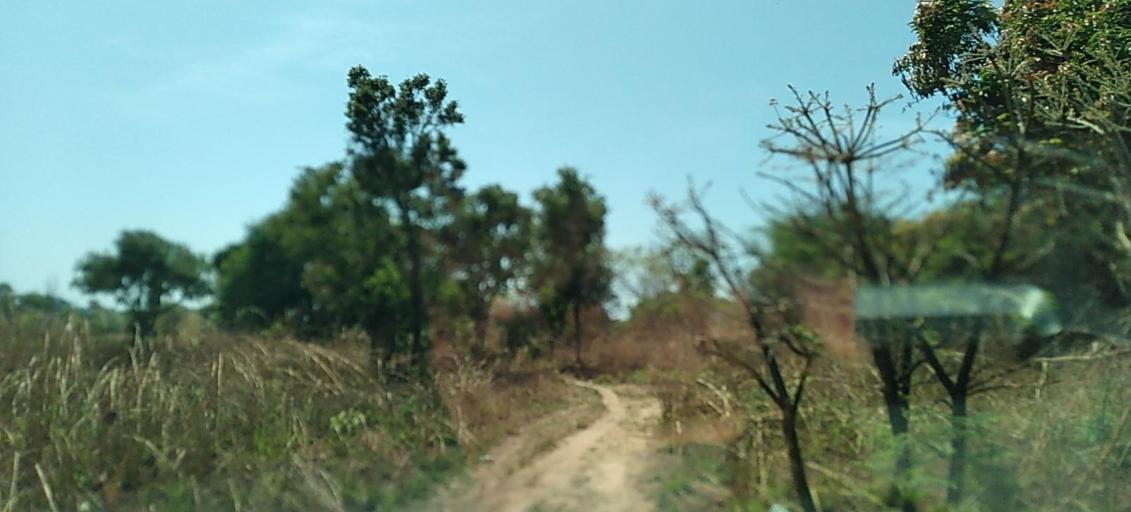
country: ZM
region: Copperbelt
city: Chililabombwe
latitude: -12.2904
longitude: 27.8935
